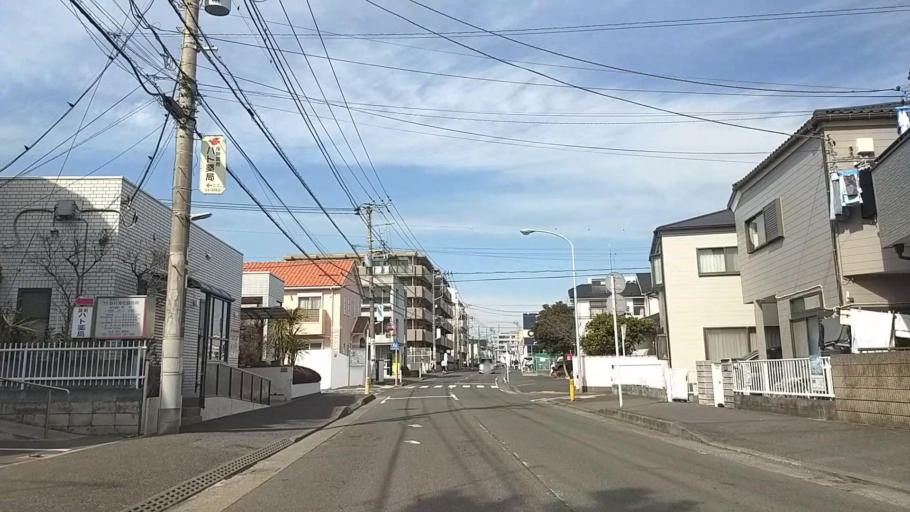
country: JP
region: Kanagawa
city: Chigasaki
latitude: 35.3257
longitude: 139.4372
